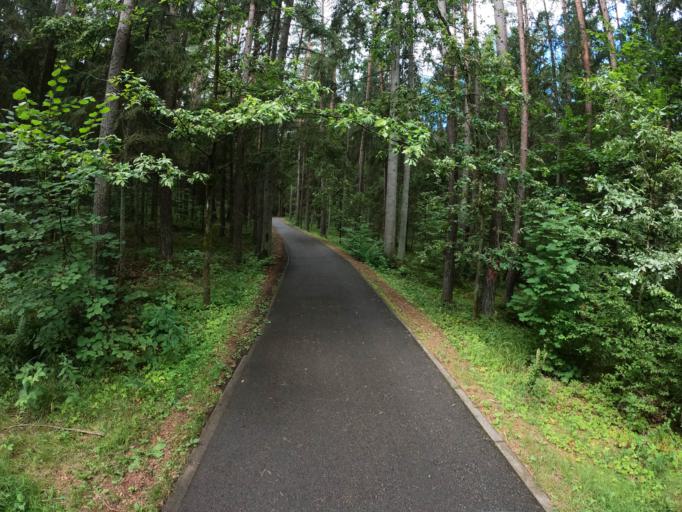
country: LT
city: Prienai
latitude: 54.6351
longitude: 23.9736
